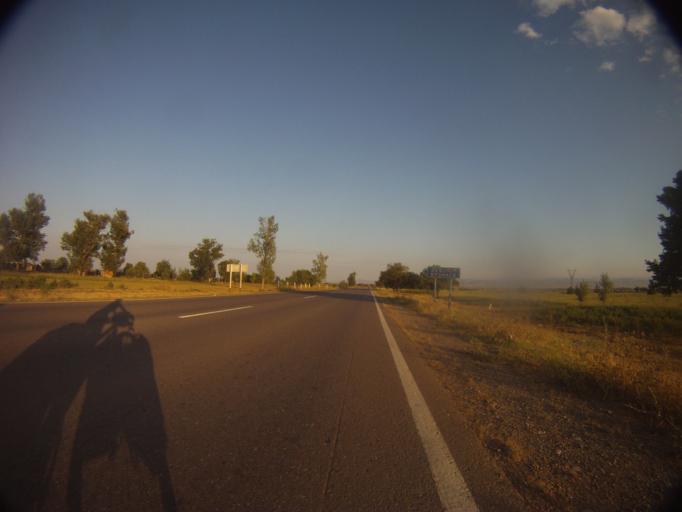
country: GE
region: Kvemo Kartli
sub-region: Gardabani
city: Gardabani
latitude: 41.3920
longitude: 45.0358
